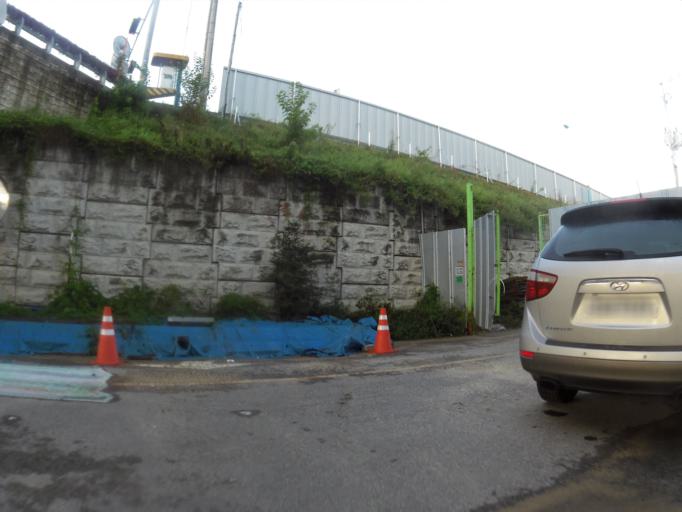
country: KR
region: Gyeongsangnam-do
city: Naeso
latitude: 35.3859
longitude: 128.4735
